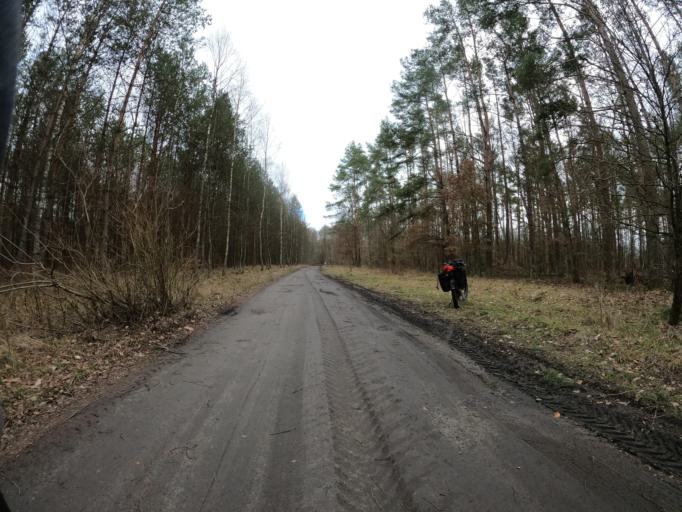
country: PL
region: Greater Poland Voivodeship
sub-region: Powiat zlotowski
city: Sypniewo
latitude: 53.4530
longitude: 16.5371
